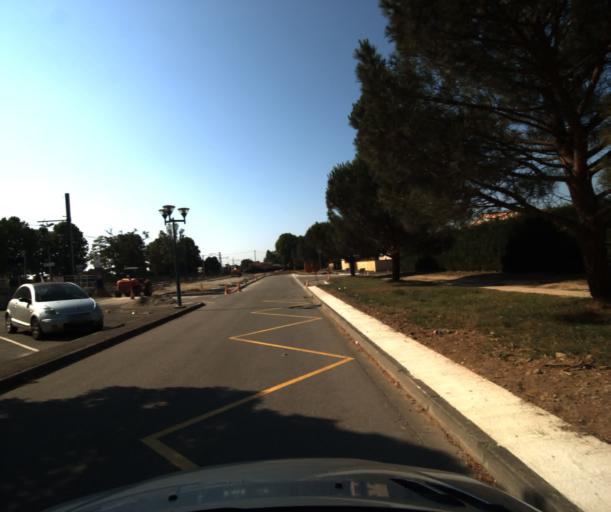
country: FR
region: Midi-Pyrenees
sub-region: Departement de la Haute-Garonne
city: Lacroix-Falgarde
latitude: 43.4793
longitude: 1.3999
